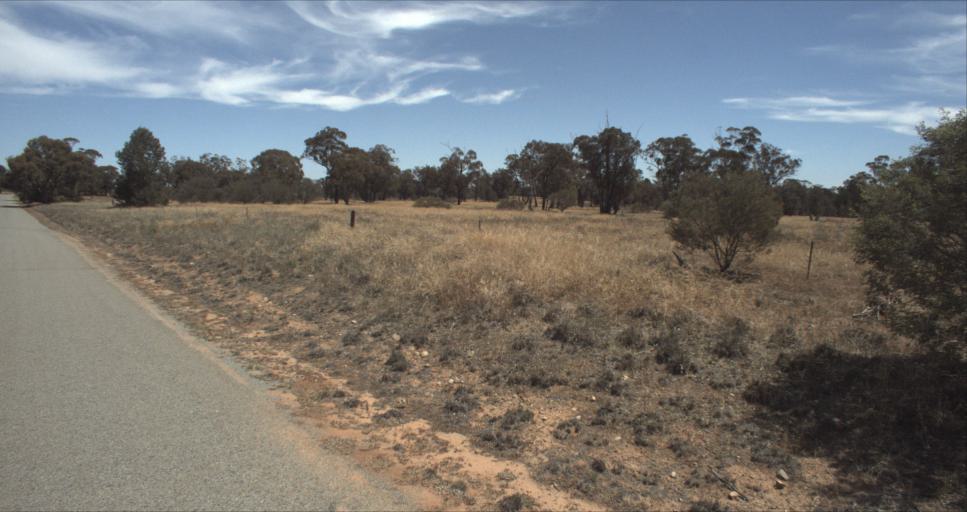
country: AU
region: New South Wales
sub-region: Leeton
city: Leeton
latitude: -34.6750
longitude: 146.4430
